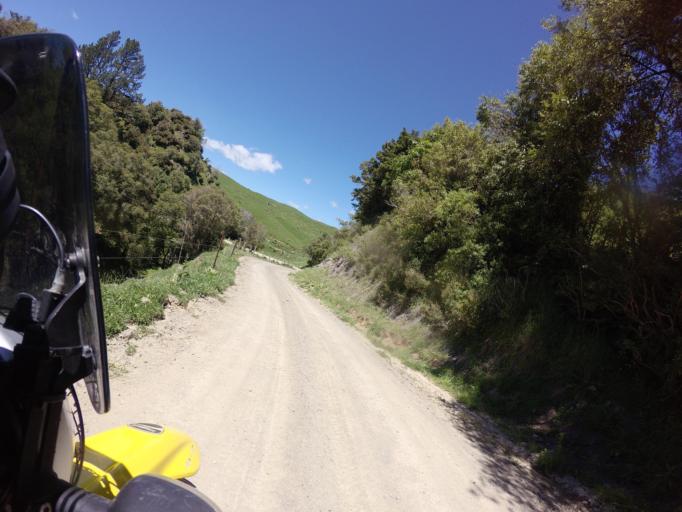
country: NZ
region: Bay of Plenty
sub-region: Opotiki District
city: Opotiki
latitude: -38.4044
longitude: 177.4517
